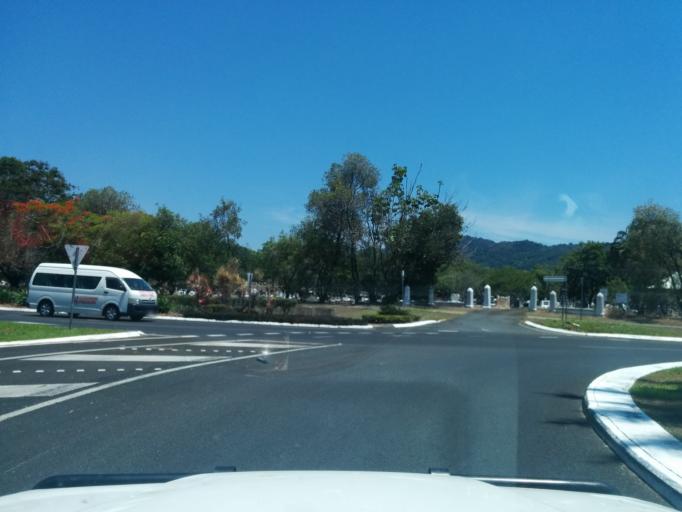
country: AU
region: Queensland
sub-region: Cairns
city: Cairns
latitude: -16.9130
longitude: 145.7546
